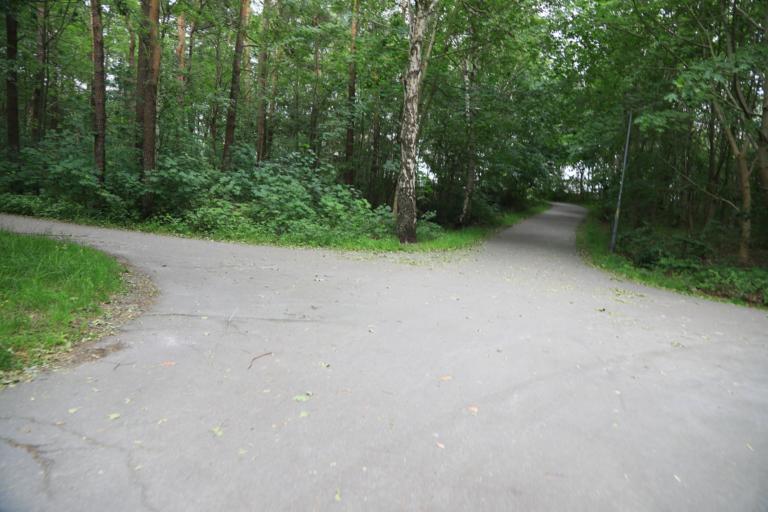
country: SE
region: Halland
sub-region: Varbergs Kommun
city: Varberg
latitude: 57.1047
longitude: 12.2856
